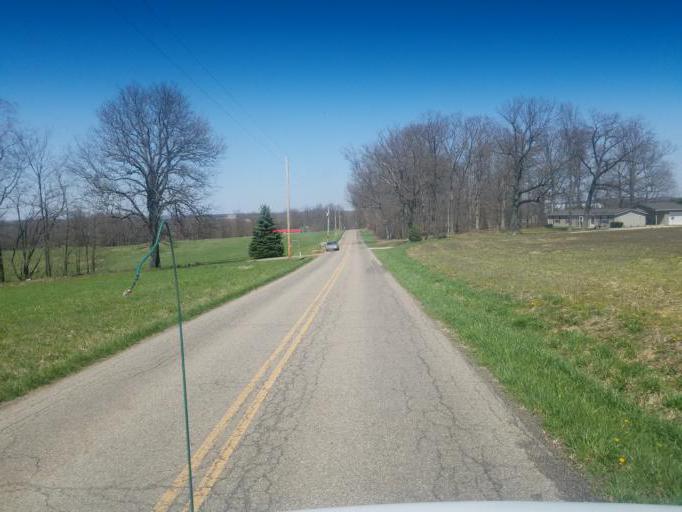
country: US
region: Ohio
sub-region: Knox County
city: Oak Hill
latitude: 40.3633
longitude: -82.2743
